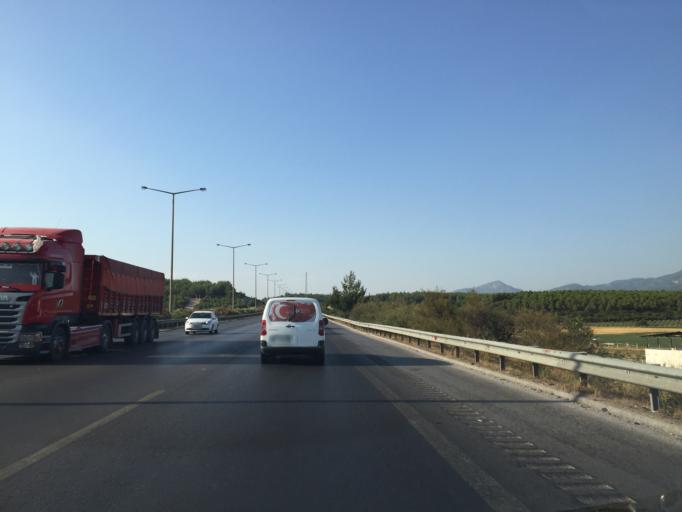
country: TR
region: Izmir
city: Menderes
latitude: 38.2806
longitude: 27.2249
